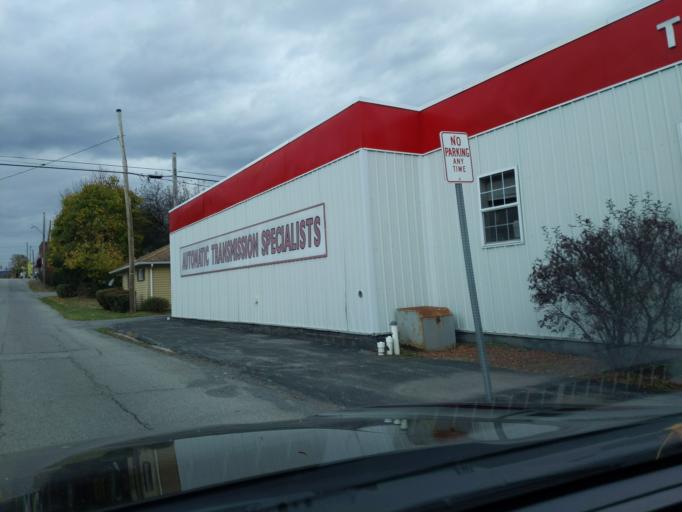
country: US
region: Pennsylvania
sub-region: Blair County
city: Altoona
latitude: 40.5196
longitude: -78.3754
